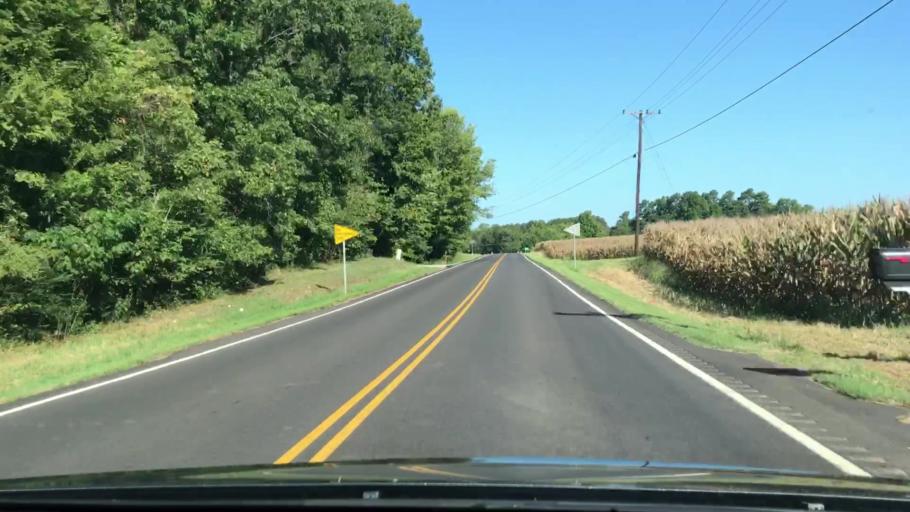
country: US
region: Kentucky
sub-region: Marshall County
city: Benton
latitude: 36.7767
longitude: -88.4445
